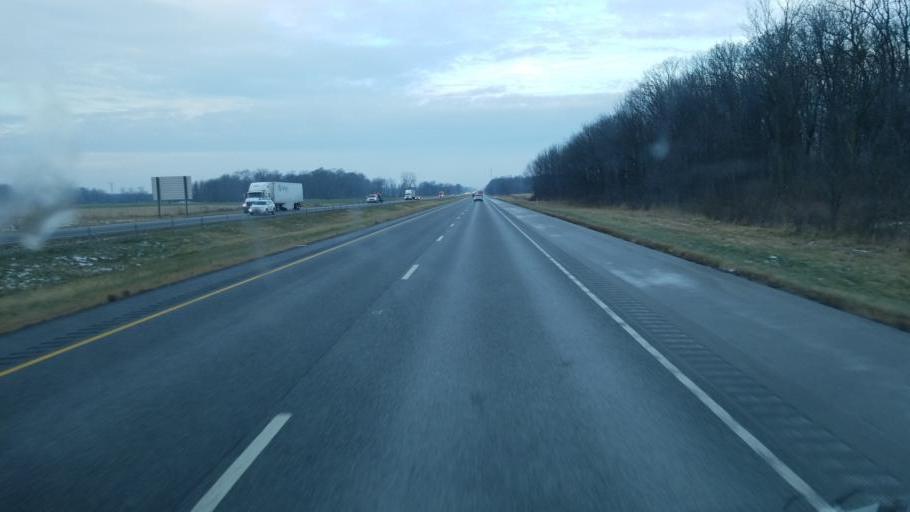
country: US
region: Indiana
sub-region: Hancock County
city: Greenfield
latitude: 39.8207
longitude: -85.8017
